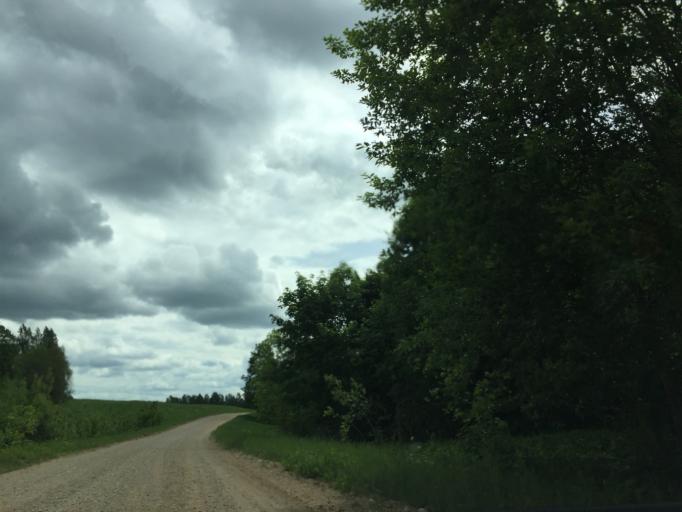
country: LV
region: Dagda
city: Dagda
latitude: 56.0448
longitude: 27.6414
